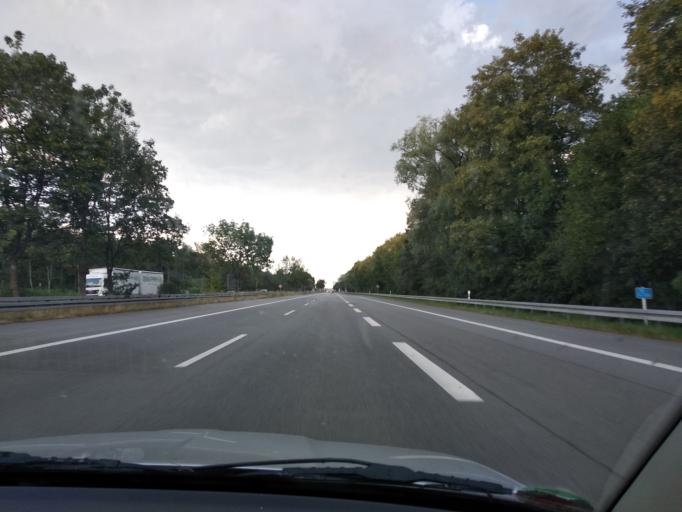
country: DE
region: Bavaria
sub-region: Upper Bavaria
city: Unterhaching
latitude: 48.0867
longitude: 11.5934
